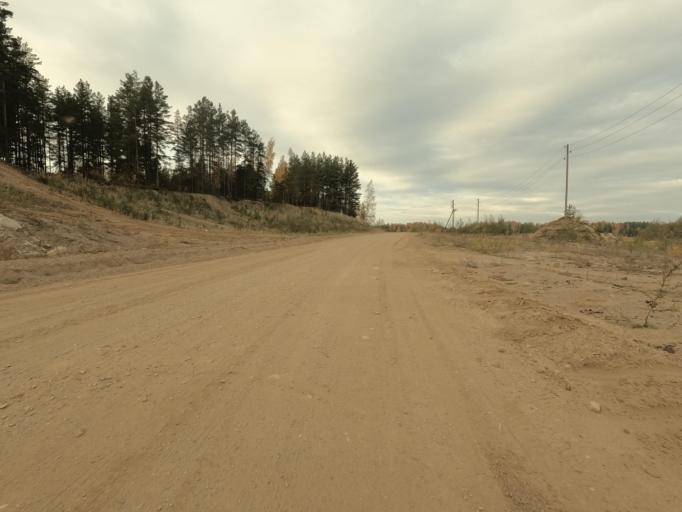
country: RU
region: Leningrad
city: Priladozhskiy
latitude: 59.7081
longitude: 31.3636
